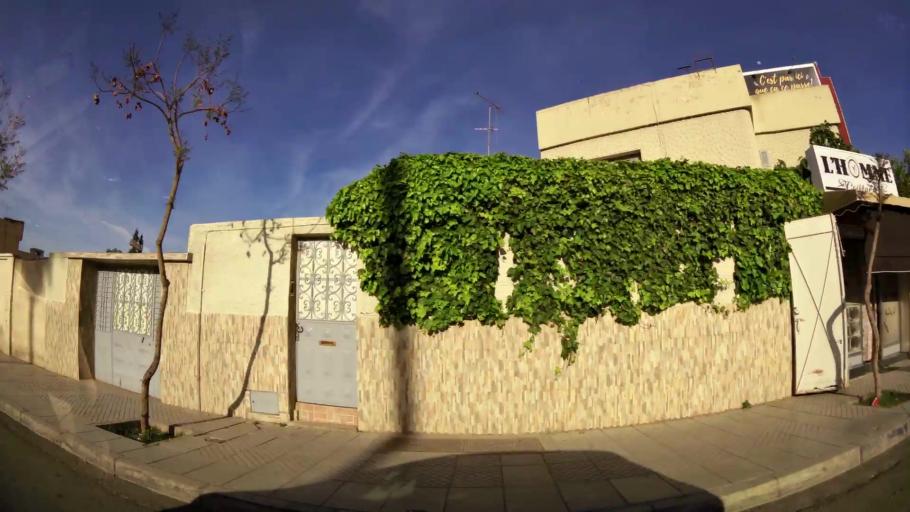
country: MA
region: Oriental
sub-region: Oujda-Angad
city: Oujda
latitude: 34.6734
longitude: -1.9125
